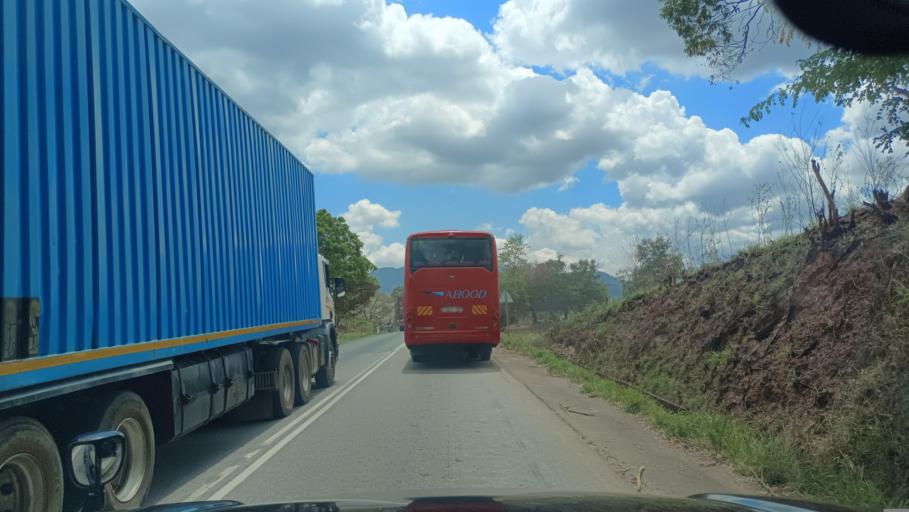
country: TZ
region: Morogoro
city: Mikumi
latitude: -7.4625
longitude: 36.9191
